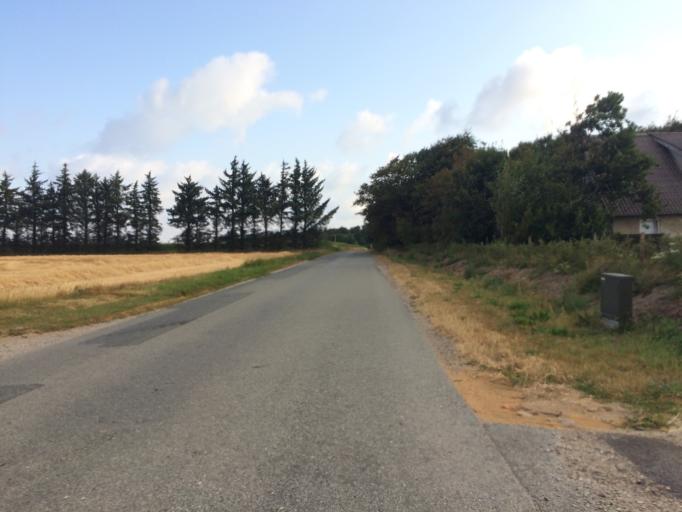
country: DK
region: Central Jutland
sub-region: Holstebro Kommune
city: Vinderup
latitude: 56.6159
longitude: 8.7335
